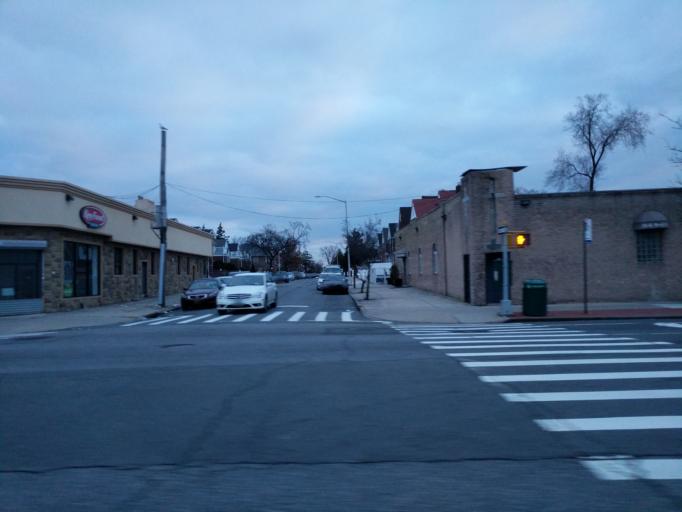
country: US
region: New York
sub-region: Nassau County
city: South Valley Stream
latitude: 40.6773
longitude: -73.7439
